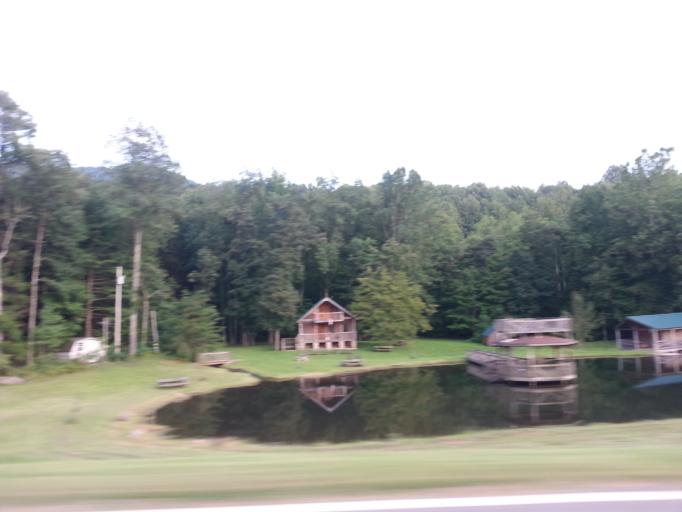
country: US
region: Tennessee
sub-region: Carter County
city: Hunter
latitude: 36.4673
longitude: -81.9992
